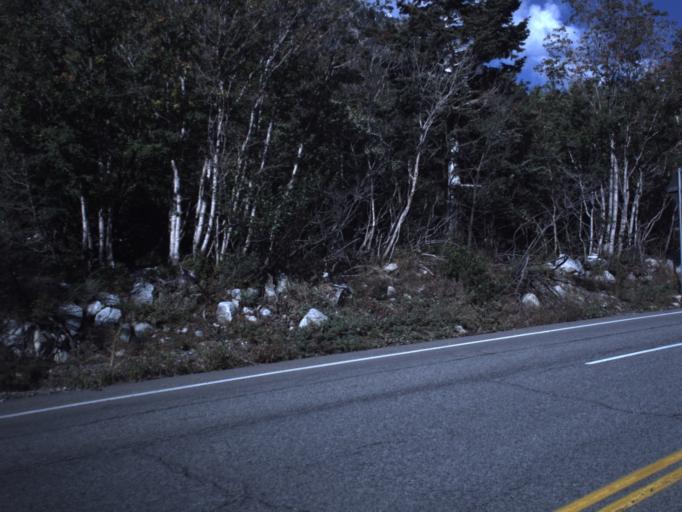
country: US
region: Utah
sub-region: Salt Lake County
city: Granite
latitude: 40.5712
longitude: -111.7073
